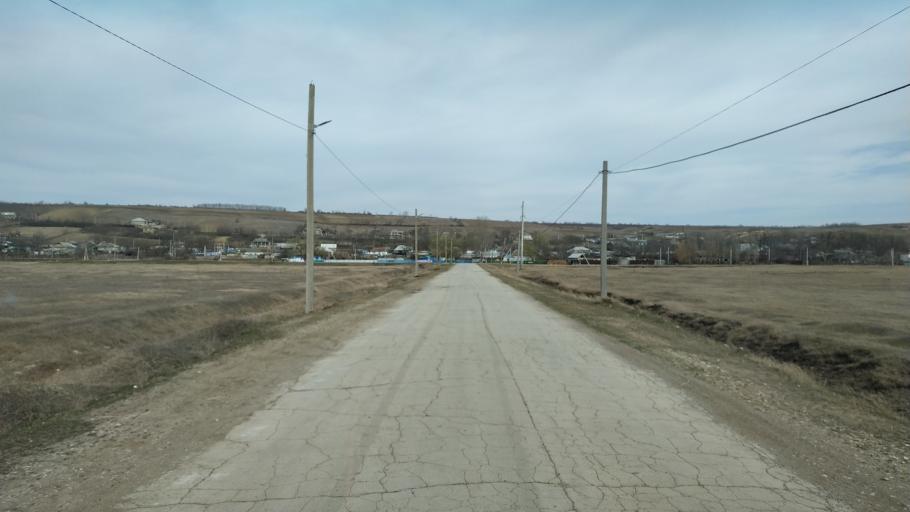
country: RO
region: Vaslui
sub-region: Comuna Dranceni
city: Dranceni
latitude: 46.8720
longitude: 28.2010
